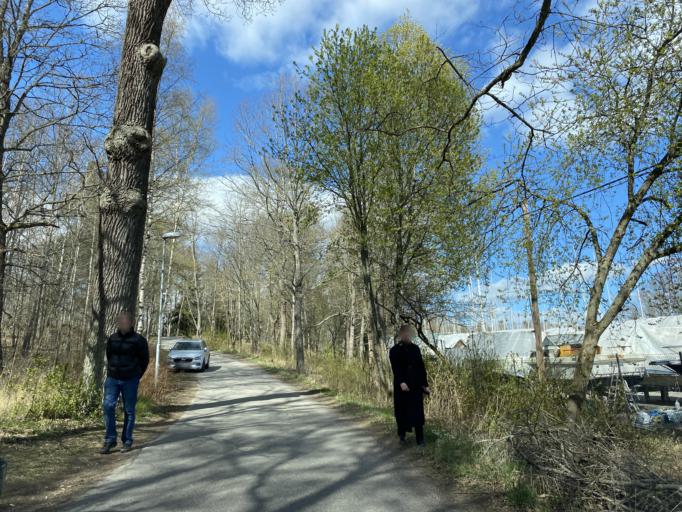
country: SE
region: Stockholm
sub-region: Nacka Kommun
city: Nacka
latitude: 59.3282
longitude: 18.1496
